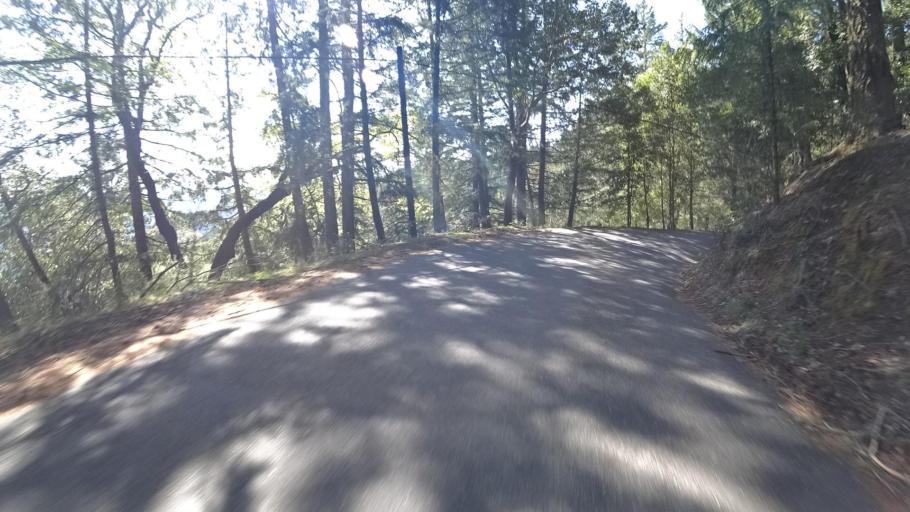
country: US
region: California
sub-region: Humboldt County
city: Redway
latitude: 40.0782
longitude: -123.6533
